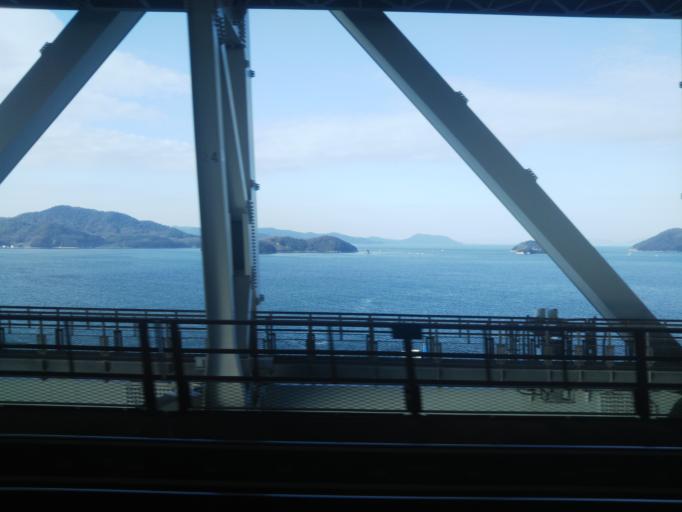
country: JP
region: Kagawa
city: Sakaidecho
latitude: 34.4108
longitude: 133.8067
